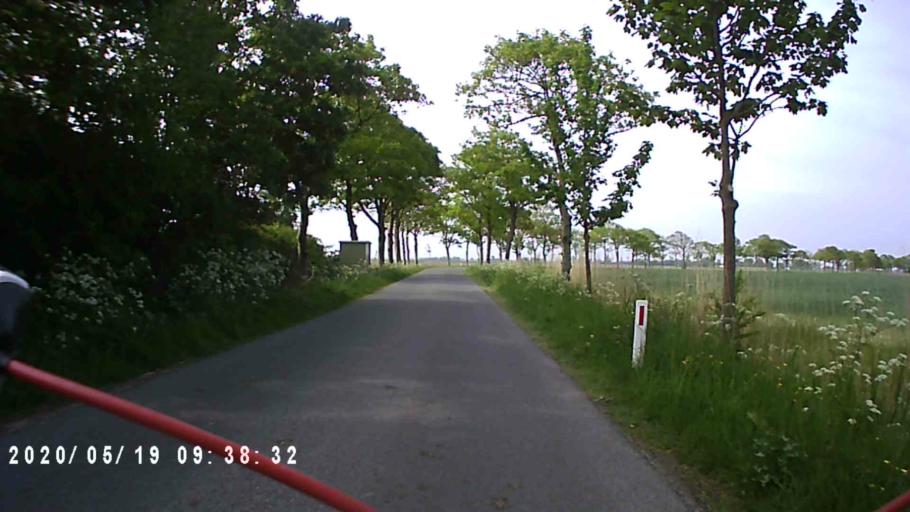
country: NL
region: Groningen
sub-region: Gemeente Zuidhorn
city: Grijpskerk
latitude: 53.2903
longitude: 6.2841
